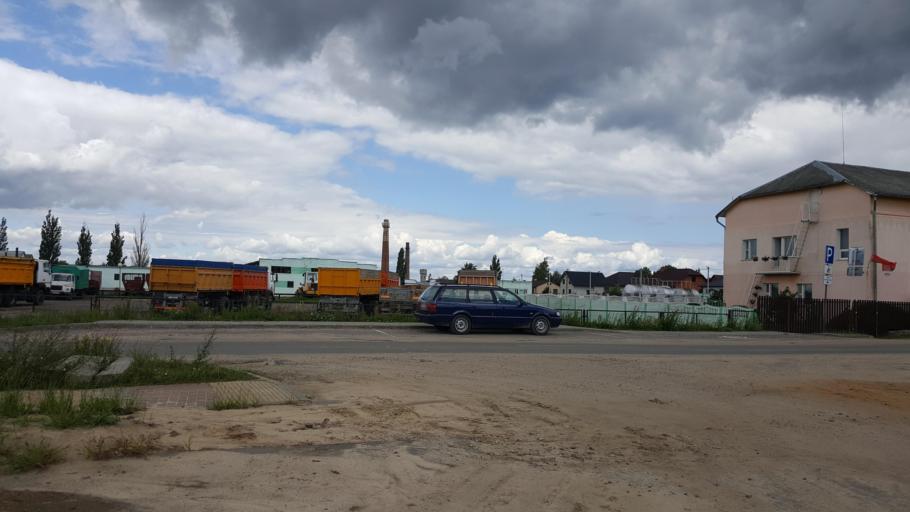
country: BY
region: Brest
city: Kamyanyets
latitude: 52.3954
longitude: 23.8350
